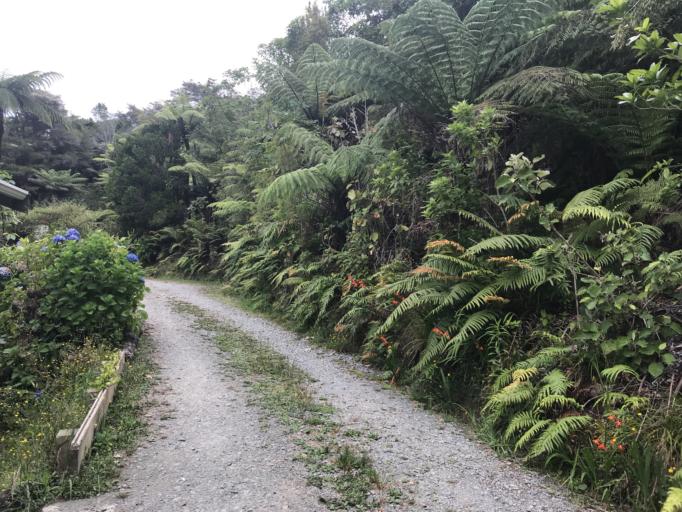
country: NZ
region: Marlborough
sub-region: Marlborough District
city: Picton
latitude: -41.2210
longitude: 173.9722
